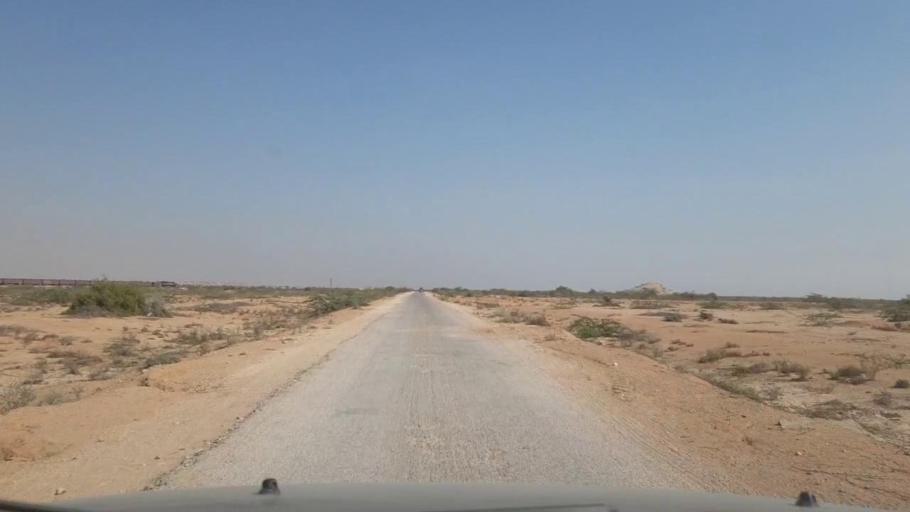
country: PK
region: Sindh
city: Thatta
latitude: 24.9782
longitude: 67.9805
